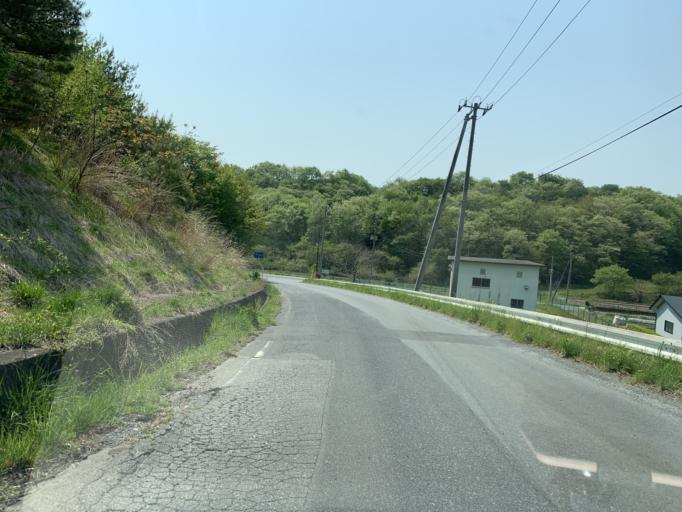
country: JP
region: Iwate
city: Ichinoseki
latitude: 38.8491
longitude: 141.0558
